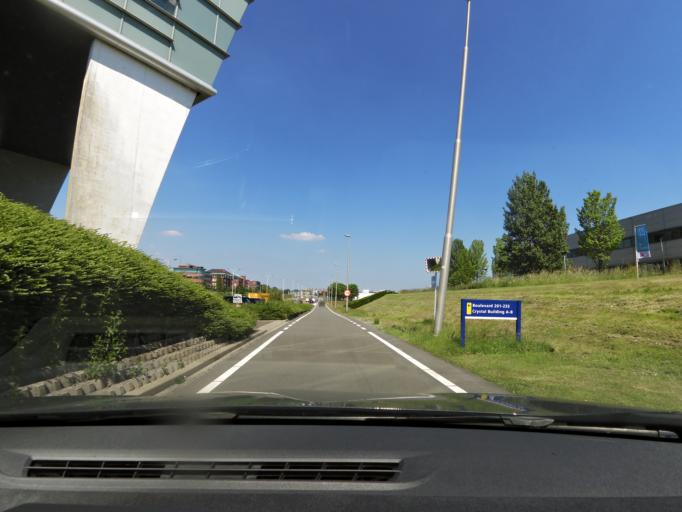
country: NL
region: South Holland
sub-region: Gemeente Rotterdam
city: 's-Gravenland
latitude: 51.9137
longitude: 4.5473
